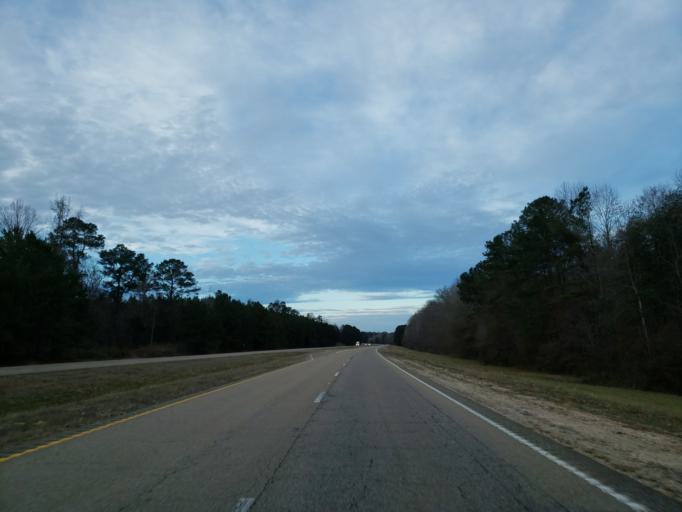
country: US
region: Mississippi
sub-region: Lauderdale County
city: Meridian Station
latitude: 32.5929
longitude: -88.5009
